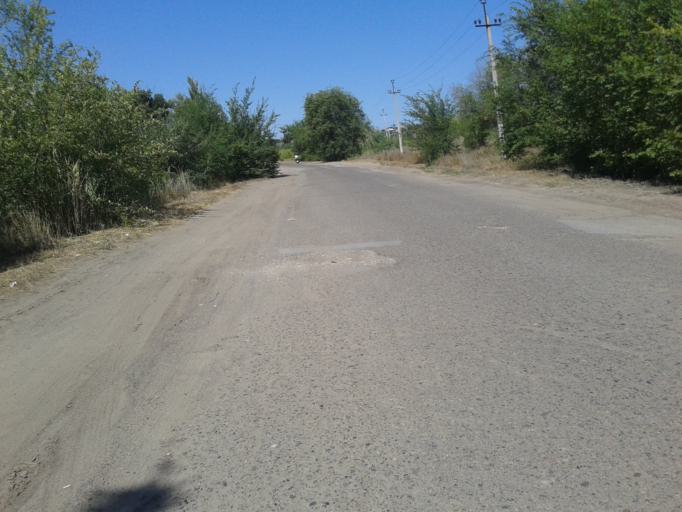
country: RU
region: Volgograd
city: Volgograd
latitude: 48.6922
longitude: 44.4416
